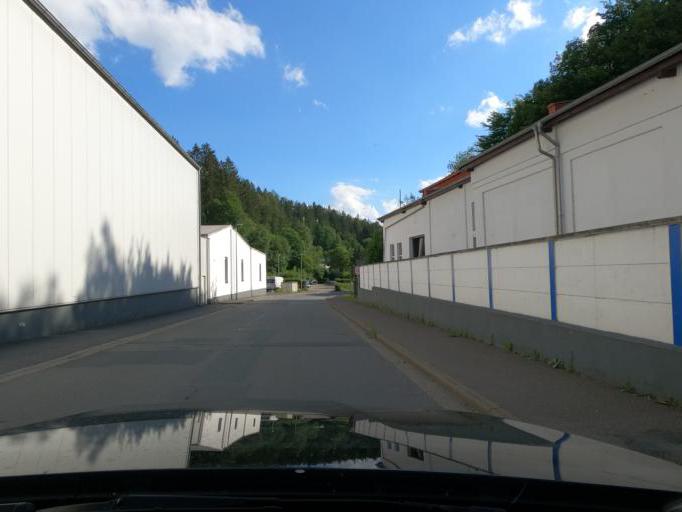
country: DE
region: Lower Saxony
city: Osterode am Harz
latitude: 51.7451
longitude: 10.2876
